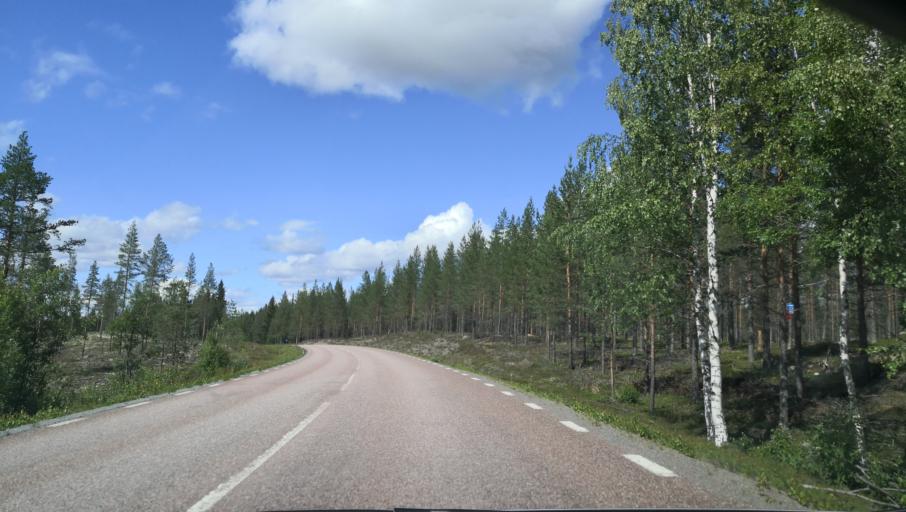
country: NO
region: Hedmark
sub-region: Trysil
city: Innbygda
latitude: 61.7651
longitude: 12.9578
